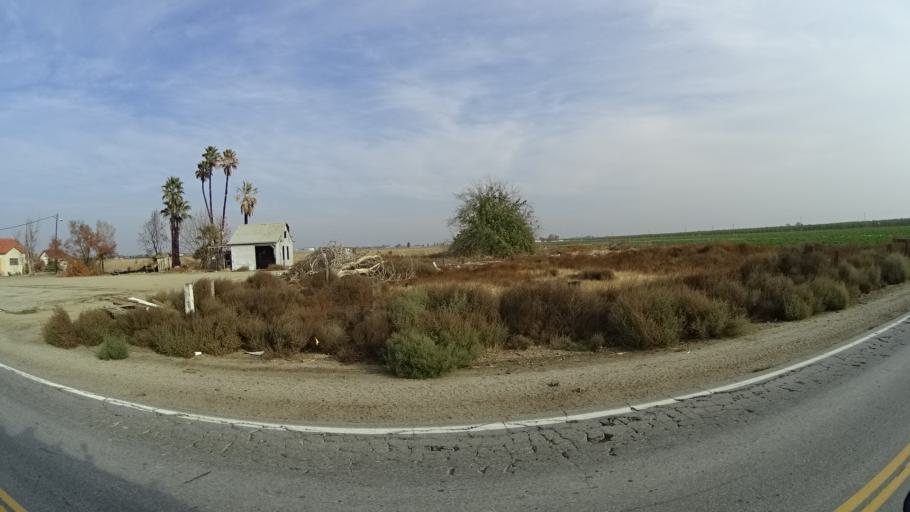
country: US
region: California
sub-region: Kern County
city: Greenacres
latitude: 35.2839
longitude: -119.1283
